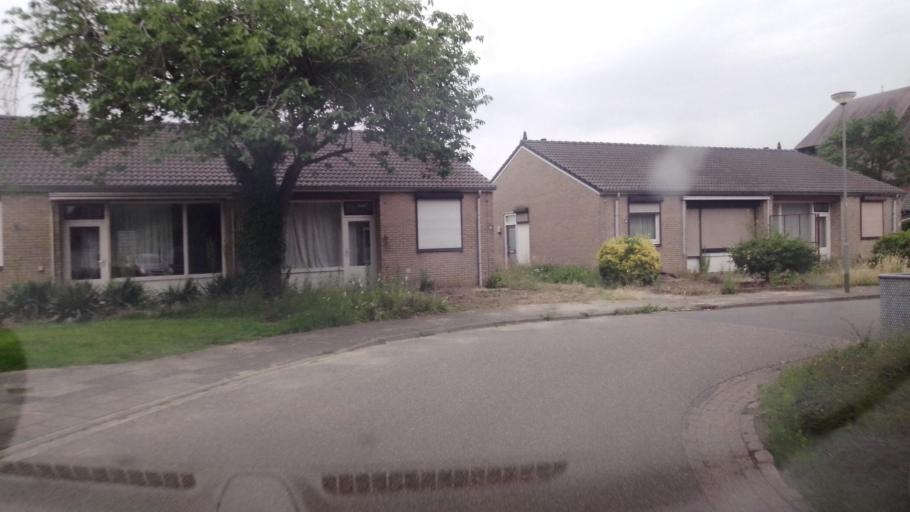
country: NL
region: Limburg
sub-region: Gemeente Venlo
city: Venlo
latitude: 51.4208
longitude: 6.1496
